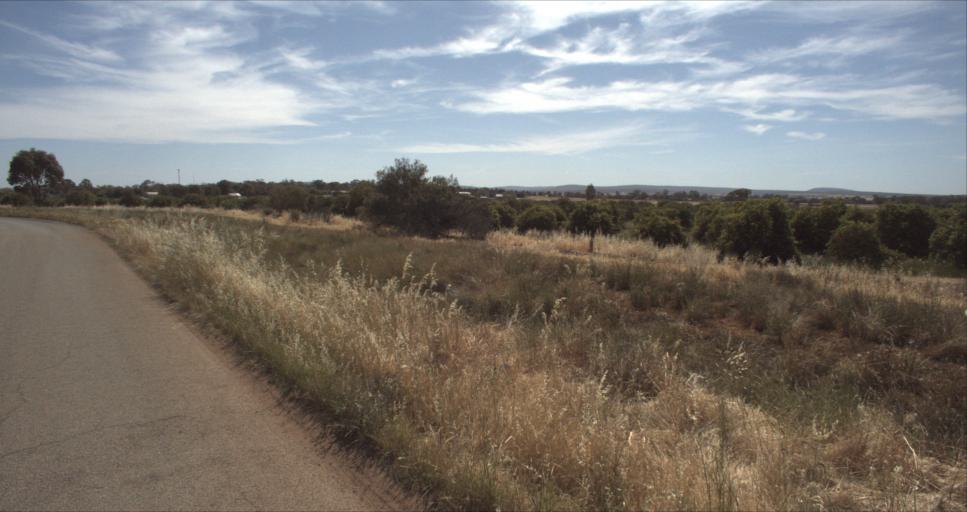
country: AU
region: New South Wales
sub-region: Leeton
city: Leeton
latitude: -34.5758
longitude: 146.4555
